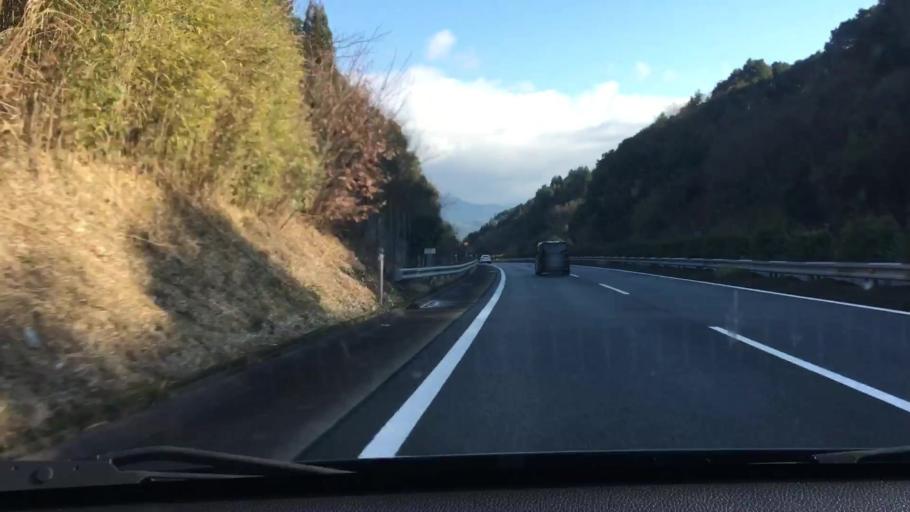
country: JP
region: Kumamoto
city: Hitoyoshi
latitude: 32.1840
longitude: 130.7793
